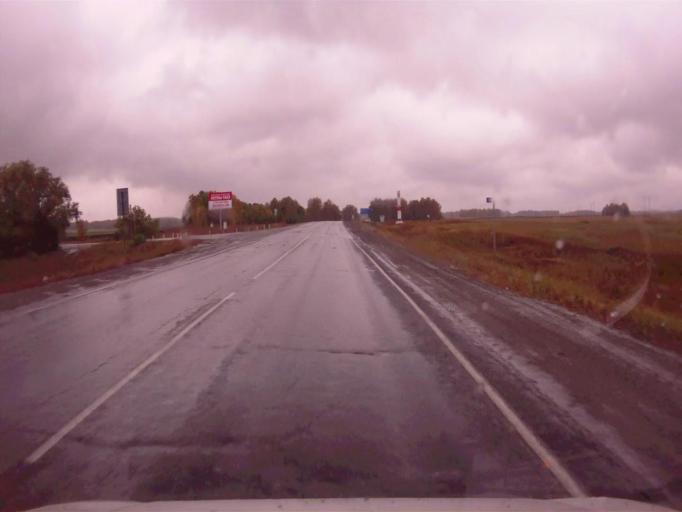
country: RU
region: Chelyabinsk
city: Roshchino
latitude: 55.3938
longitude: 61.1077
